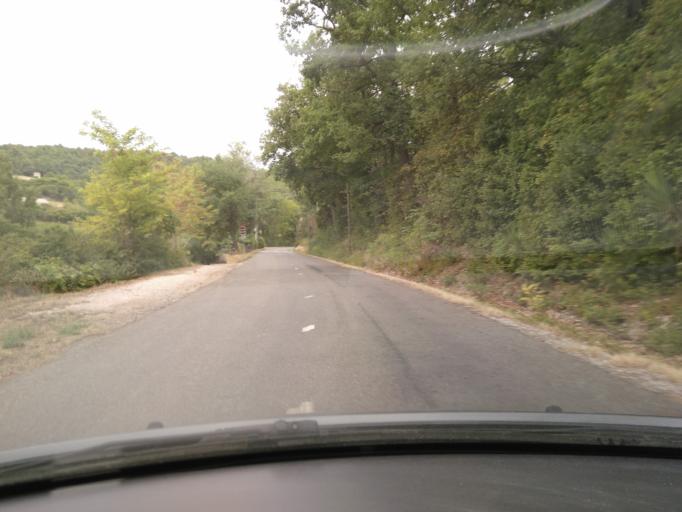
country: FR
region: Rhone-Alpes
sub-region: Departement de la Drome
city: Vinsobres
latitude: 44.3374
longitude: 5.0582
